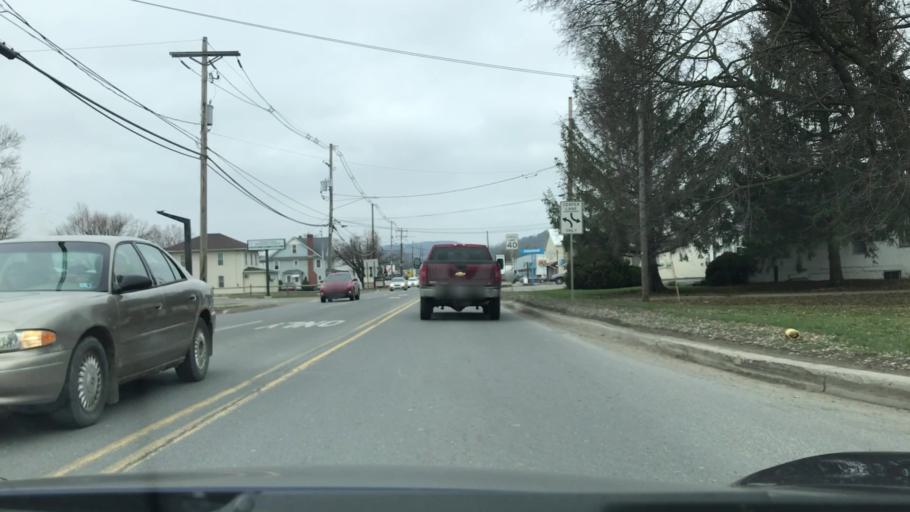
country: US
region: Pennsylvania
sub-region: Bradford County
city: Towanda
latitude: 41.7742
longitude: -76.3997
